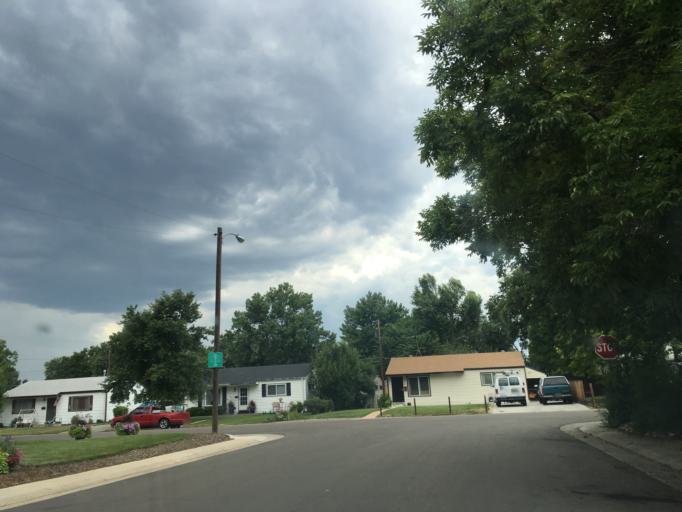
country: US
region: Colorado
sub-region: Arapahoe County
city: Sheridan
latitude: 39.6725
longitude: -105.0276
